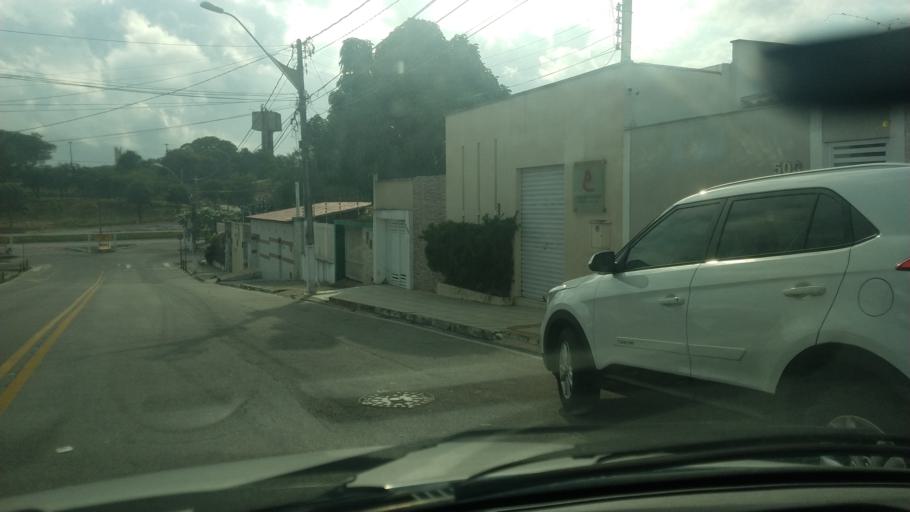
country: BR
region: Rio Grande do Norte
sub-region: Natal
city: Natal
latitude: -5.8417
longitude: -35.2046
